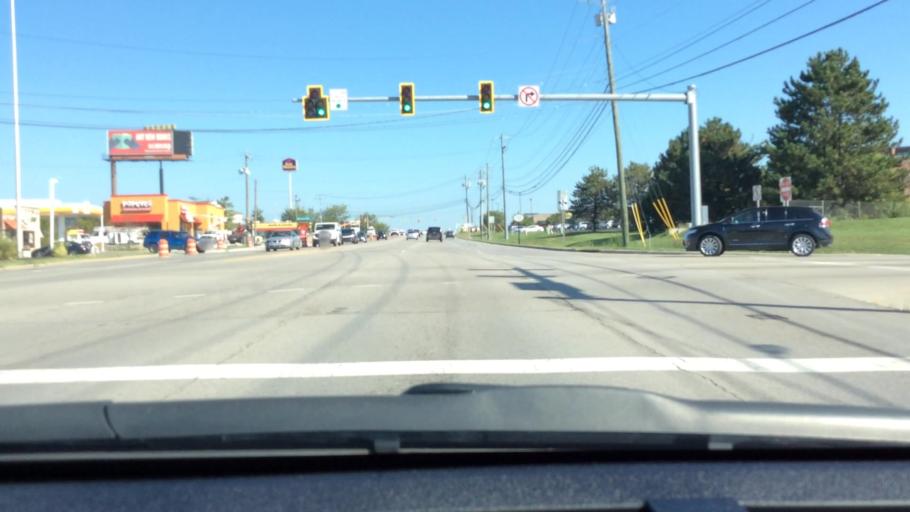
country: US
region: Ohio
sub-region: Hamilton County
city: Sixteen Mile Stand
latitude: 39.2951
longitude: -84.3153
